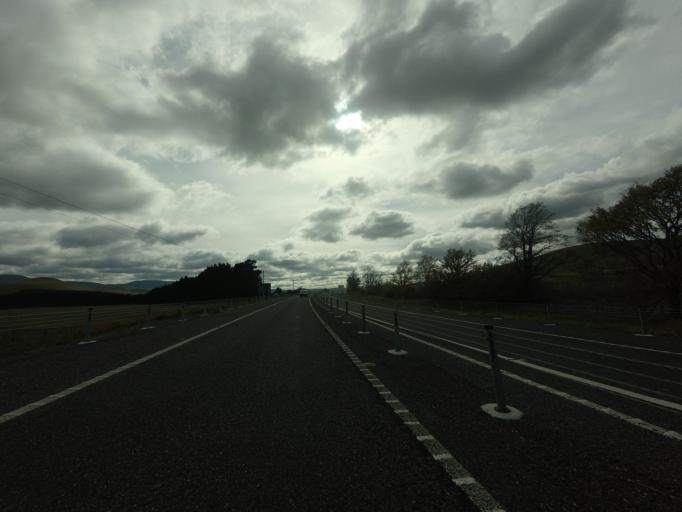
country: AU
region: Tasmania
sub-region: Brighton
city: Bridgewater
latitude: -42.5172
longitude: 147.1905
